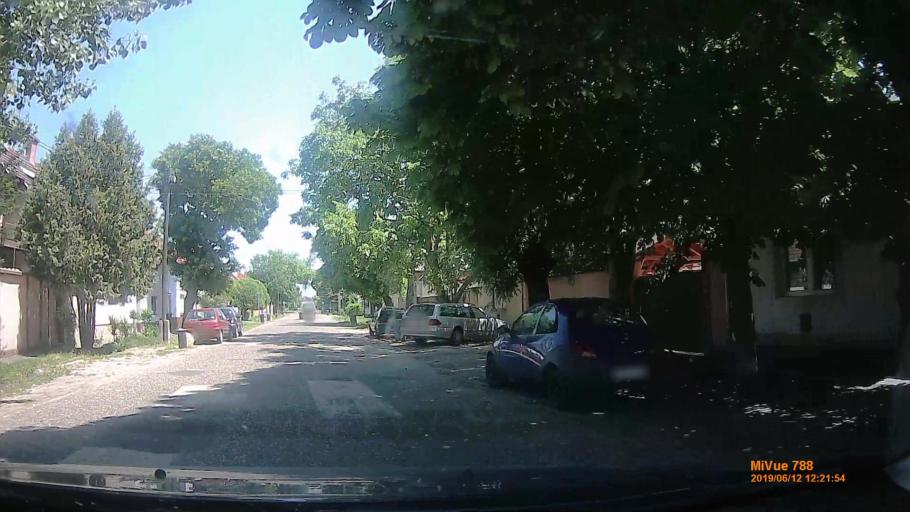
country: HU
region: Bacs-Kiskun
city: Kecskemet
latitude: 46.8973
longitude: 19.6954
